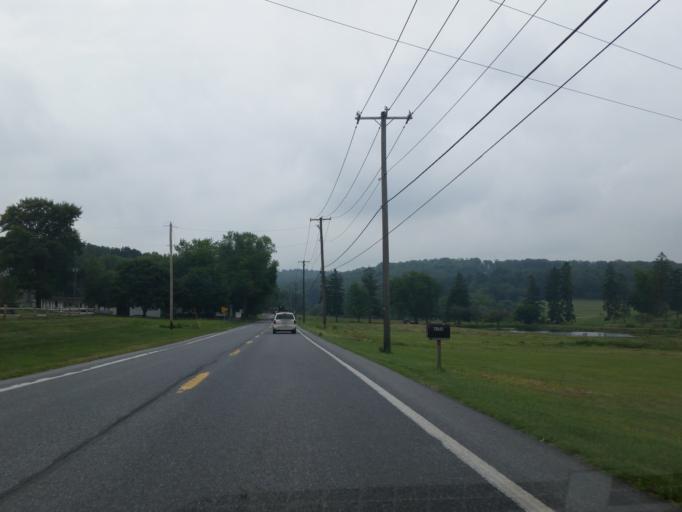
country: US
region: Pennsylvania
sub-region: Lancaster County
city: Brickerville
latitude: 40.2632
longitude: -76.3064
